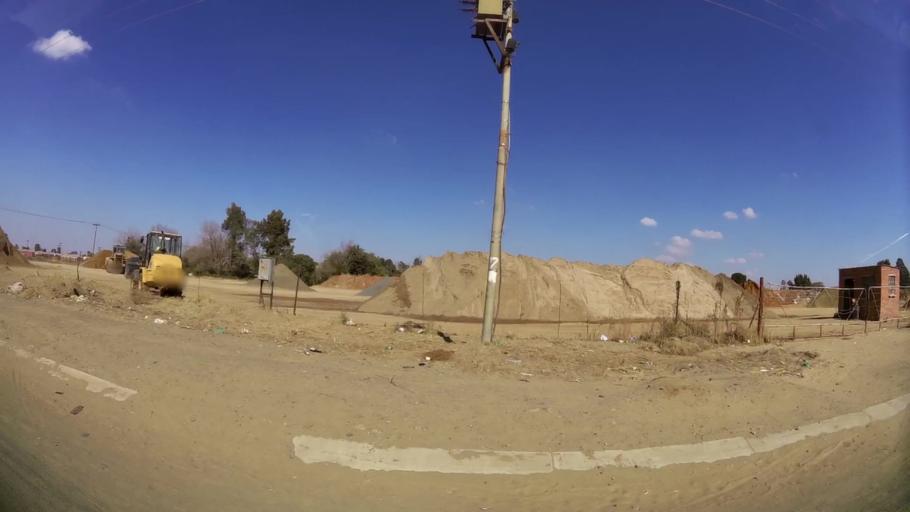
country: ZA
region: Orange Free State
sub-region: Mangaung Metropolitan Municipality
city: Bloemfontein
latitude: -29.1372
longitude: 26.2740
